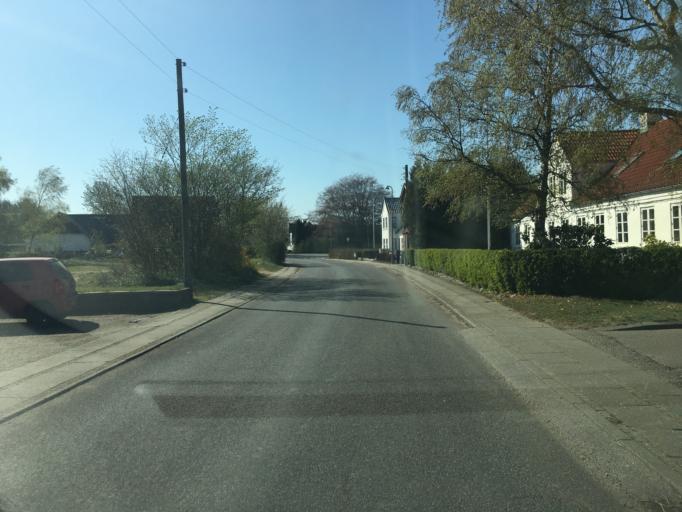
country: DK
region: South Denmark
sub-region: Aabenraa Kommune
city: Tinglev
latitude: 54.9927
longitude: 9.2939
